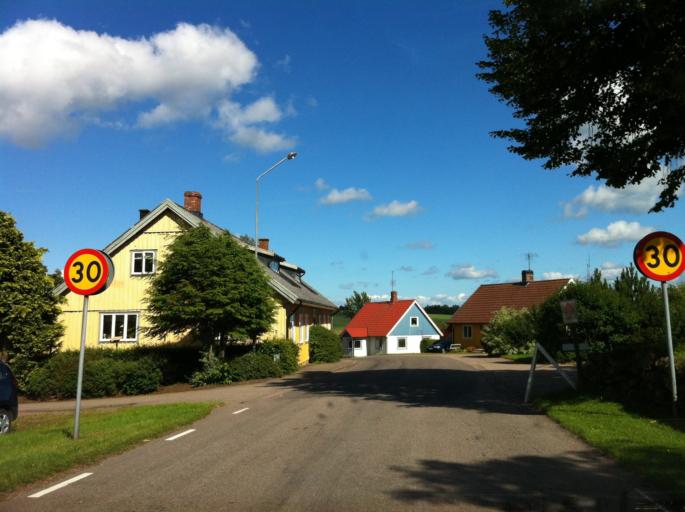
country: SE
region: Skane
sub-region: Svalovs Kommun
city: Kagerod
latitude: 56.0672
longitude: 13.0789
